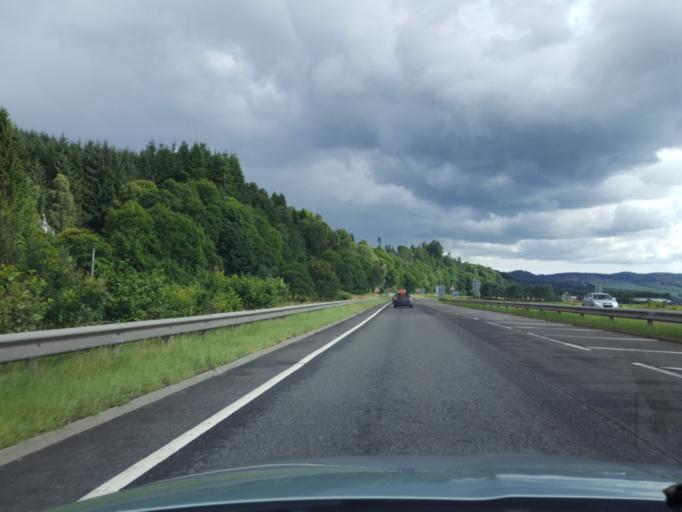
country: GB
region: Scotland
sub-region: Perth and Kinross
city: Pitlochry
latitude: 56.6470
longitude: -3.6609
